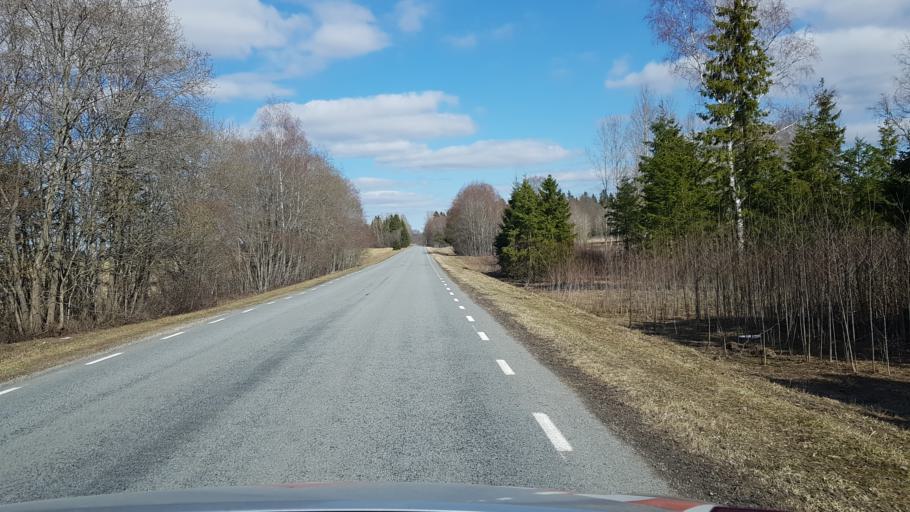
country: EE
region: Laeaene-Virumaa
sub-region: Tapa vald
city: Tapa
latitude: 59.1833
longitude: 26.0173
